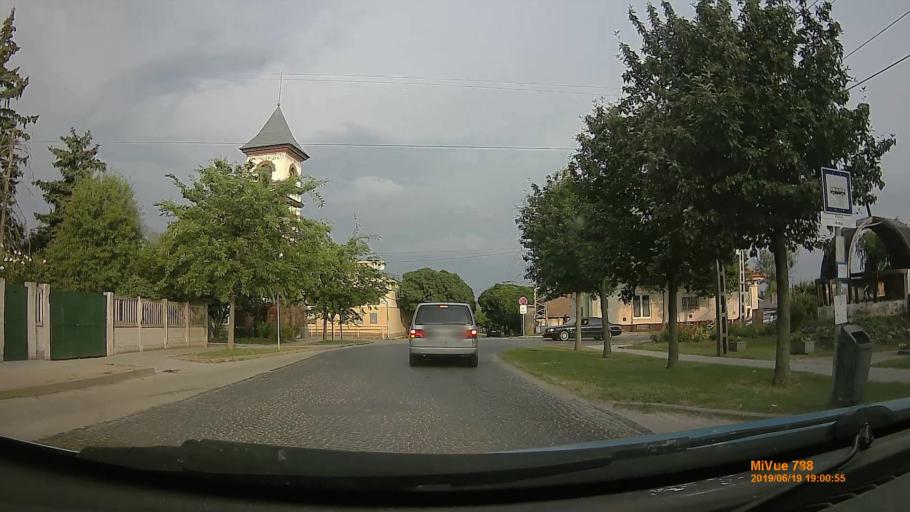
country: HU
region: Fejer
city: Ercsi
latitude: 47.2492
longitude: 18.9024
